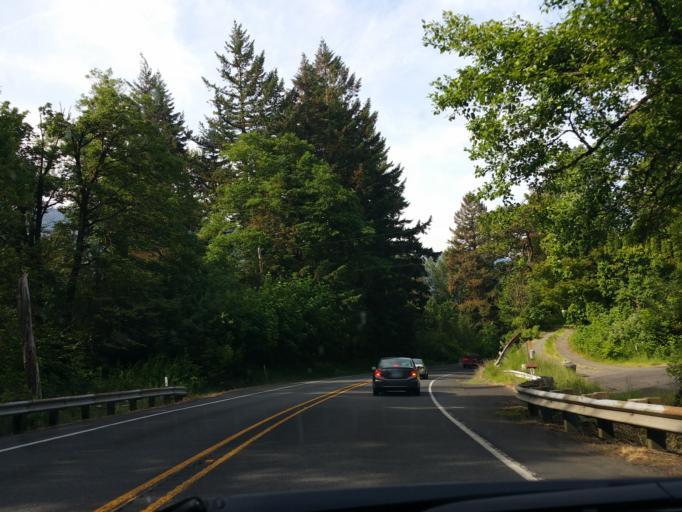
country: US
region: Oregon
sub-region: Hood River County
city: Cascade Locks
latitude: 45.6240
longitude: -122.0250
